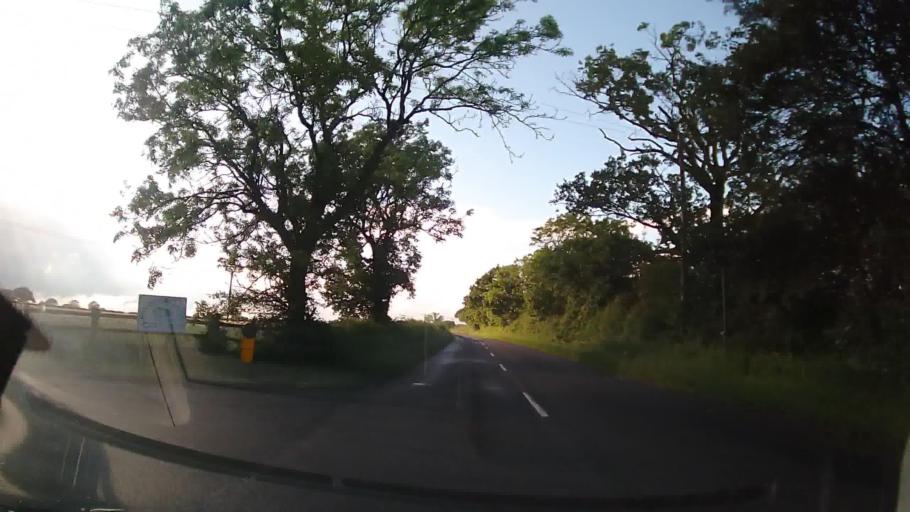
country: GB
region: England
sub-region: Leicestershire
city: Markfield
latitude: 52.6681
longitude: -1.2704
